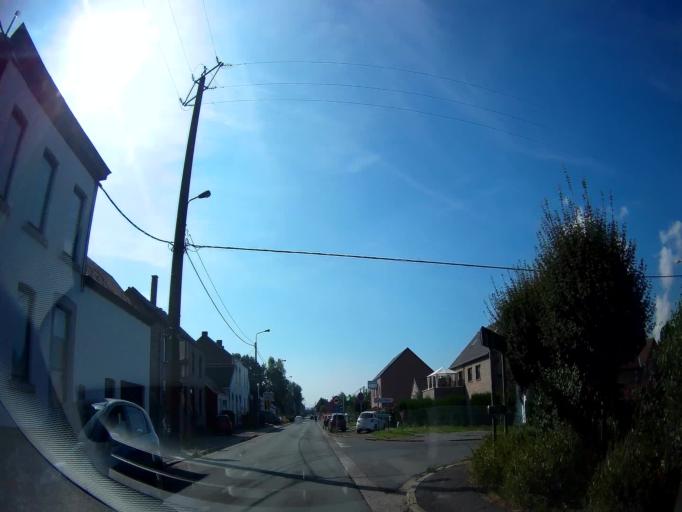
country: BE
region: Wallonia
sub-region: Province de Liege
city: Amay
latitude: 50.5584
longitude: 5.3057
